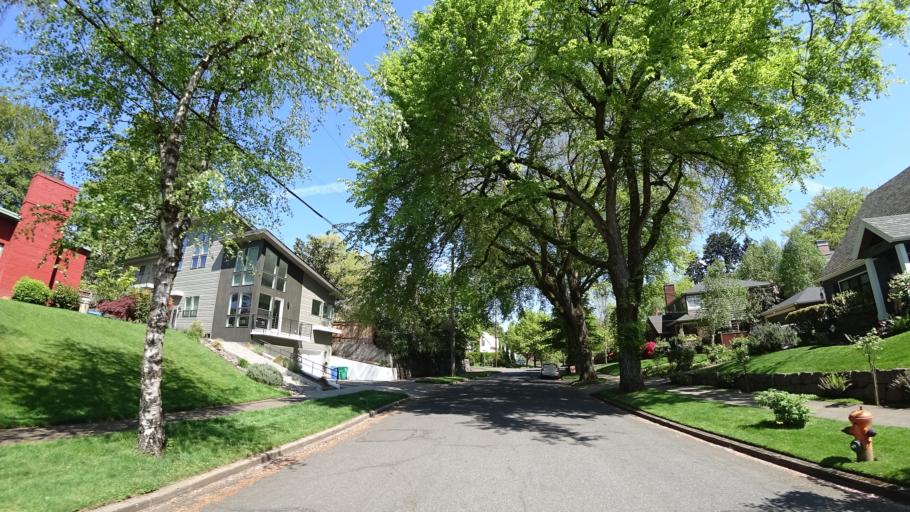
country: US
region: Oregon
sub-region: Clackamas County
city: Milwaukie
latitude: 45.4720
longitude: -122.6332
